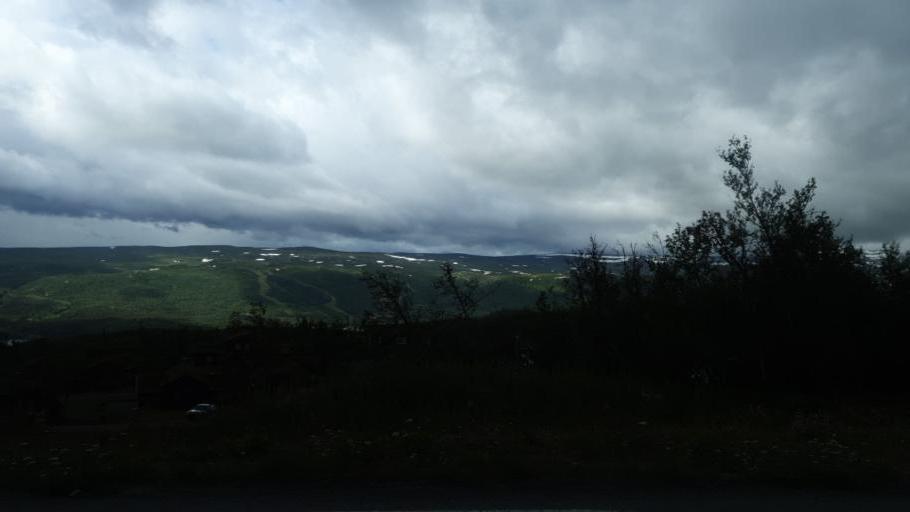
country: NO
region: Oppland
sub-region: Vestre Slidre
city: Slidre
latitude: 61.2548
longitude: 8.8775
